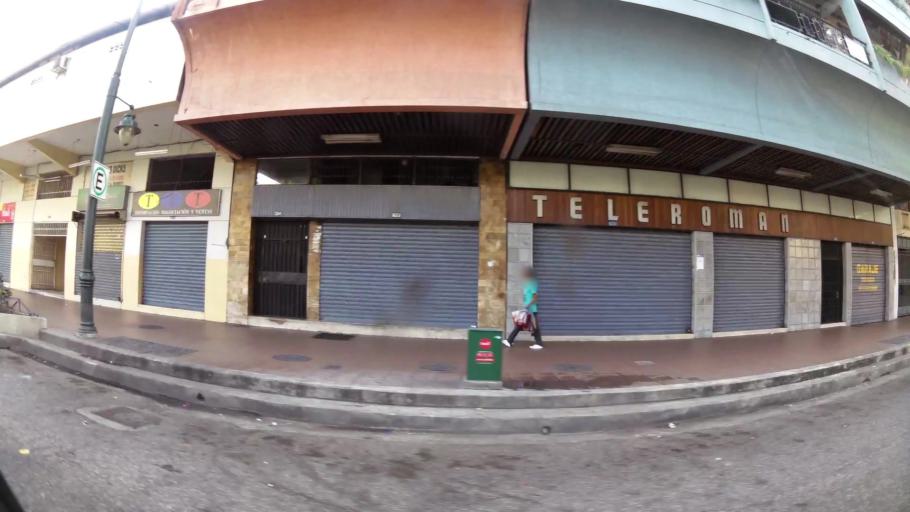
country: EC
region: Guayas
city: Guayaquil
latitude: -2.1962
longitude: -79.8858
